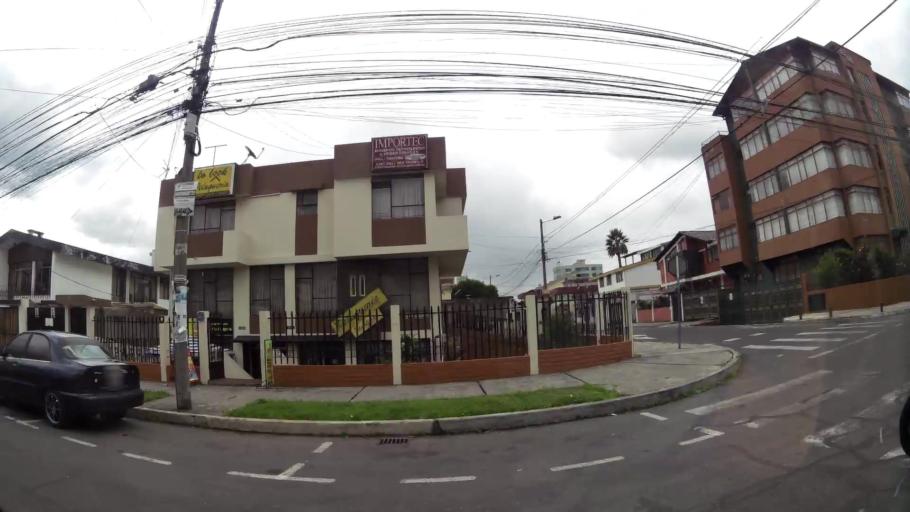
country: EC
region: Pichincha
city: Quito
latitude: -0.1731
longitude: -78.4792
